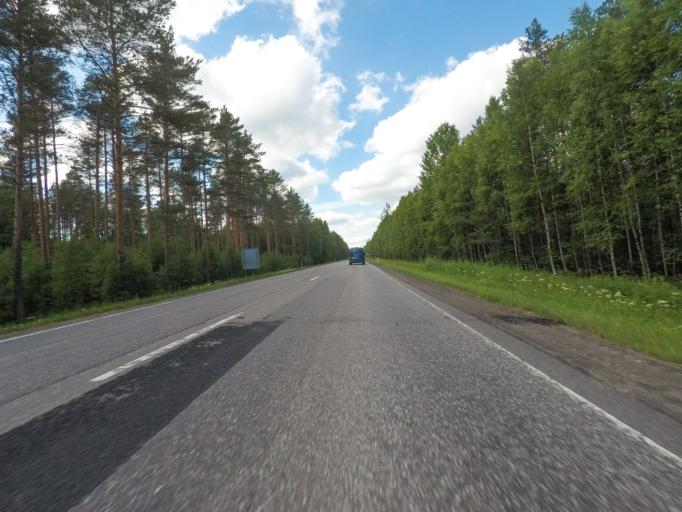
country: FI
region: Southern Savonia
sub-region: Savonlinna
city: Kerimaeki
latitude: 61.8314
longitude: 29.2305
